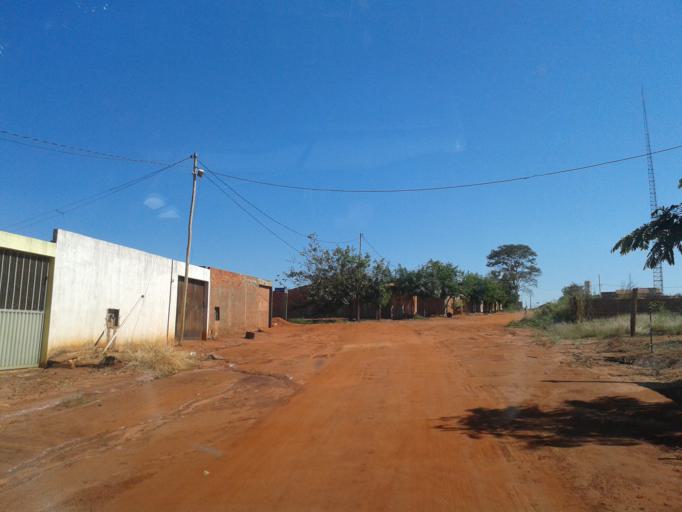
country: BR
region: Minas Gerais
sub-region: Santa Vitoria
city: Santa Vitoria
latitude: -18.8613
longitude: -50.1190
